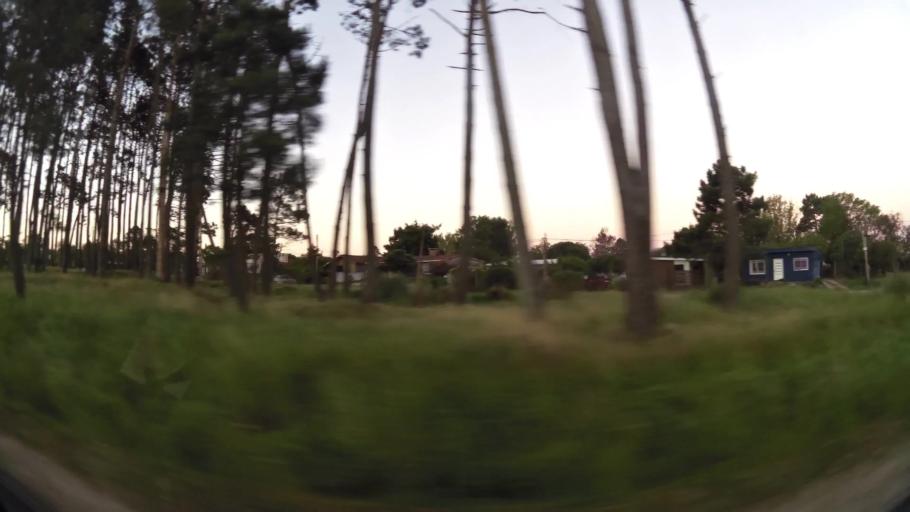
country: UY
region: Canelones
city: Colonia Nicolich
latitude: -34.8212
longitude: -55.9492
